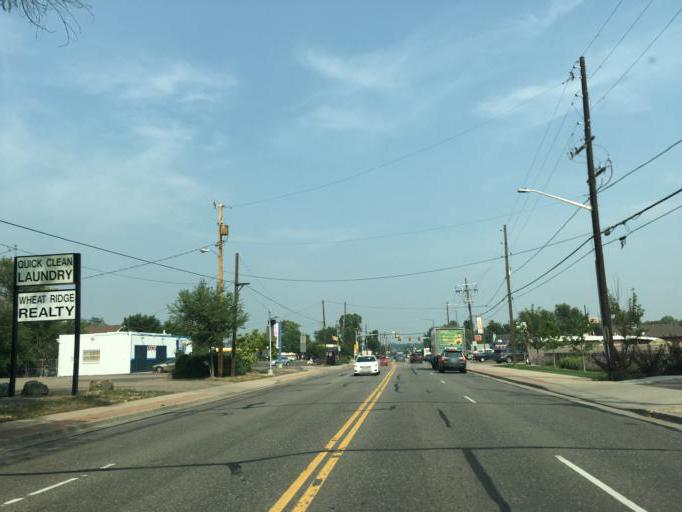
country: US
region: Colorado
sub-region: Jefferson County
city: Arvada
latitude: 39.7781
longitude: -105.1119
